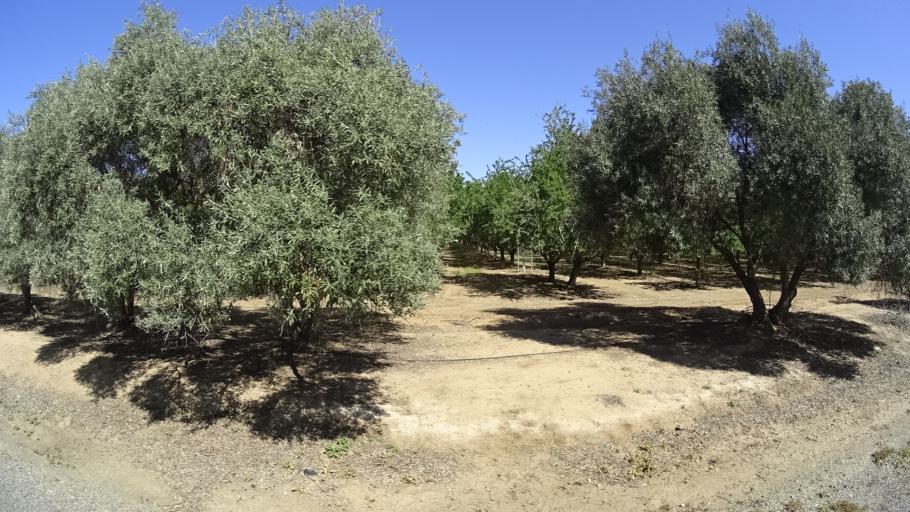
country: US
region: California
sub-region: Glenn County
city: Hamilton City
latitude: 39.7755
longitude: -122.0354
